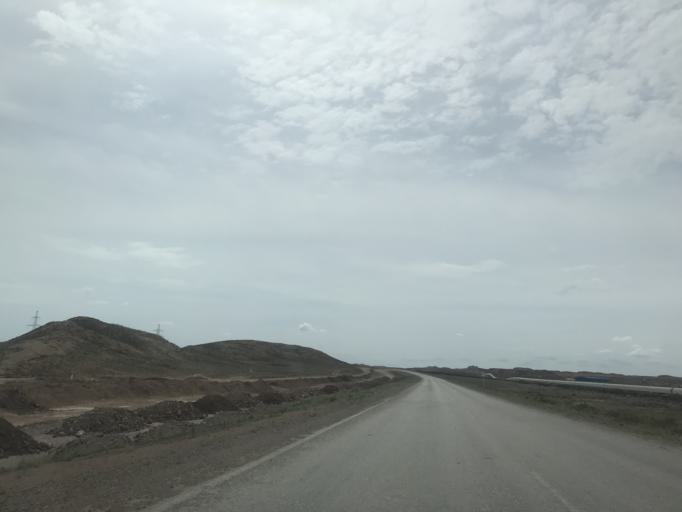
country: KZ
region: Zhambyl
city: Mynaral
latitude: 45.3738
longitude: 73.6565
